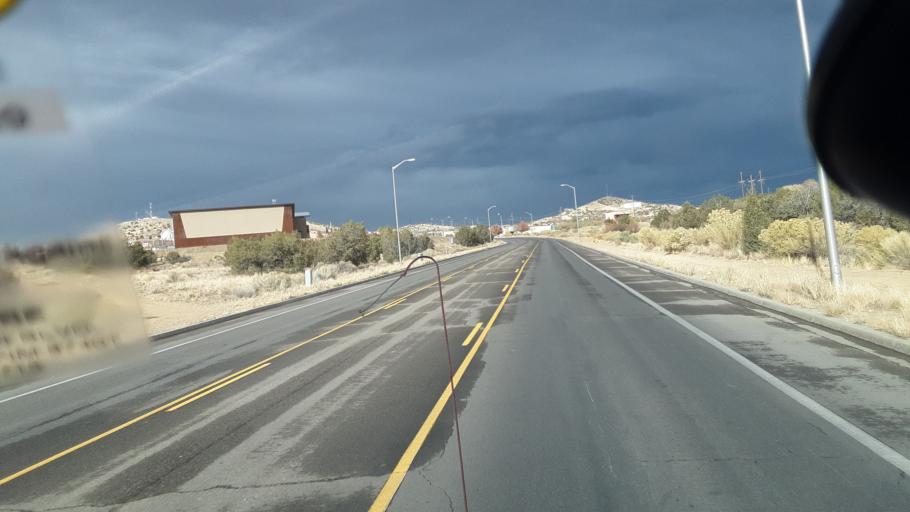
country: US
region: New Mexico
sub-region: San Juan County
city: Farmington
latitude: 36.7666
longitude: -108.1863
